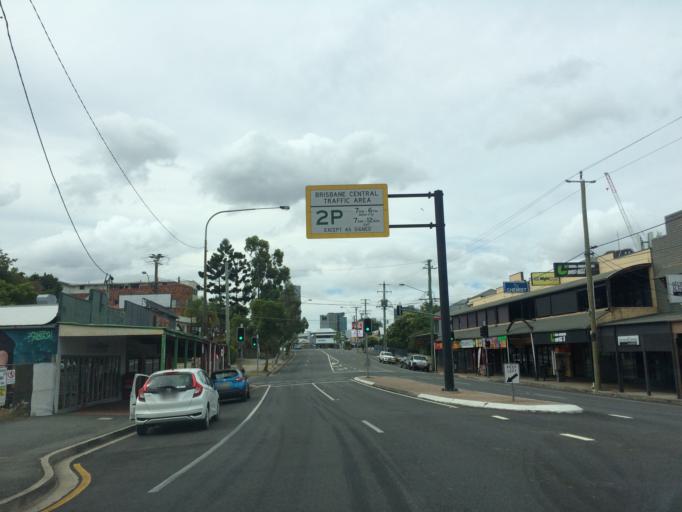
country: AU
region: Queensland
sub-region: Brisbane
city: South Brisbane
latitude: -27.4851
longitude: 153.0196
